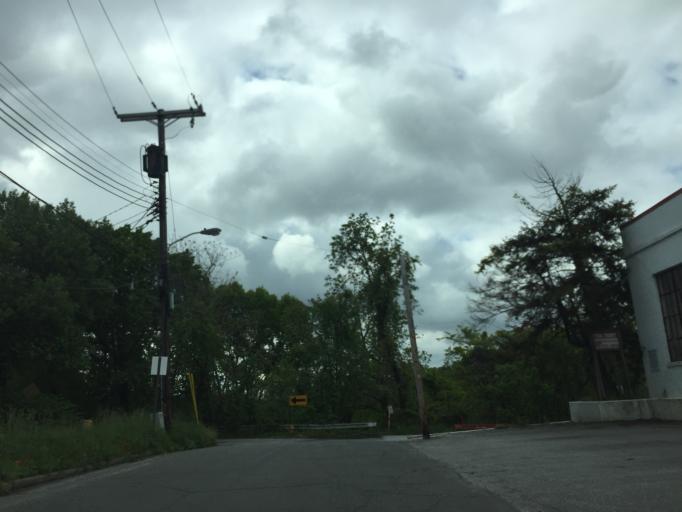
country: US
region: Maryland
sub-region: City of Baltimore
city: Baltimore
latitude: 39.3257
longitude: -76.6321
